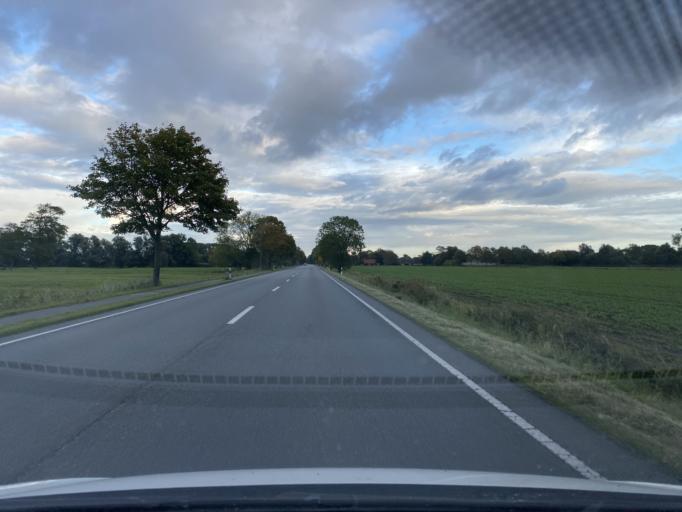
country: DE
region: Lower Saxony
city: Nordleda
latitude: 53.7997
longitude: 8.8482
